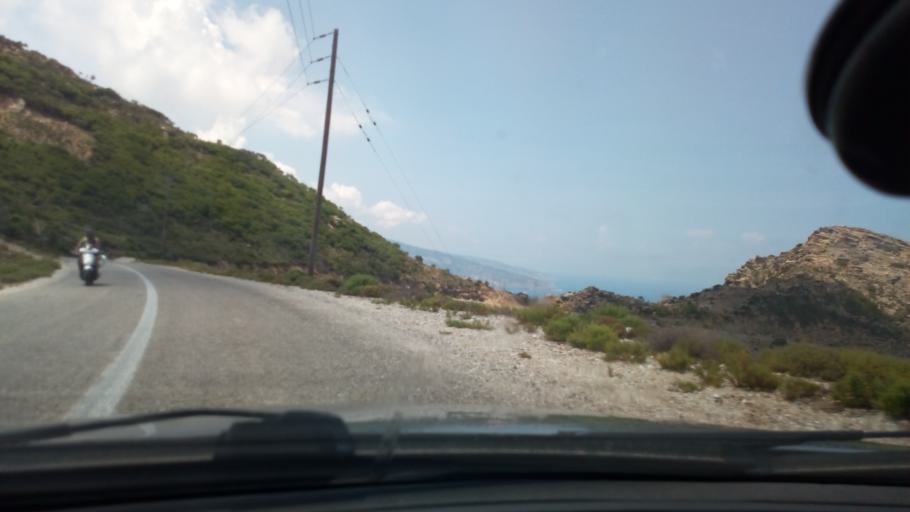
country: GR
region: North Aegean
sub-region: Nomos Samou
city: Agios Kirykos
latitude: 37.6402
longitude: 26.2527
